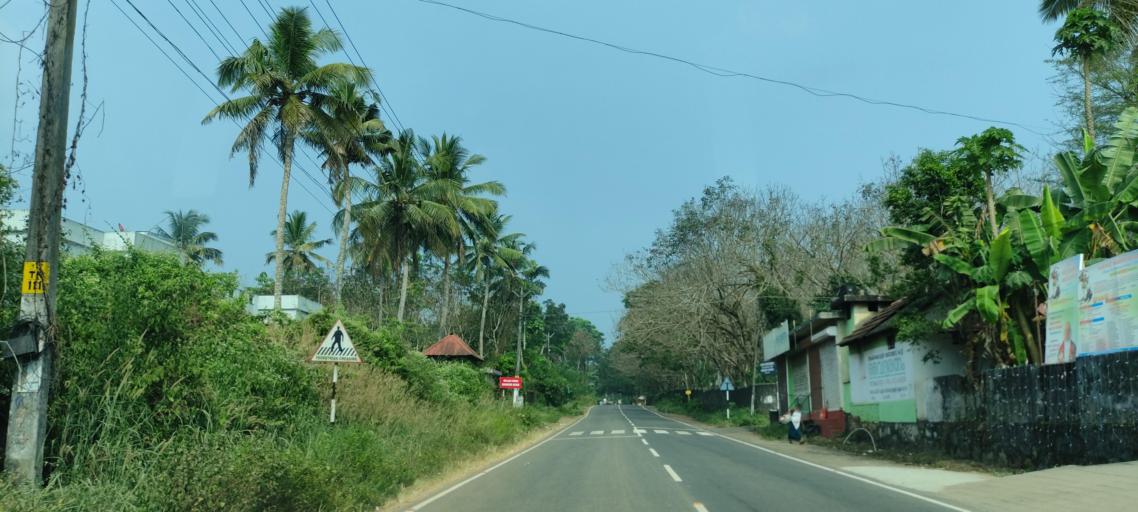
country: IN
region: Kerala
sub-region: Ernakulam
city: Piravam
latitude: 9.7957
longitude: 76.4703
